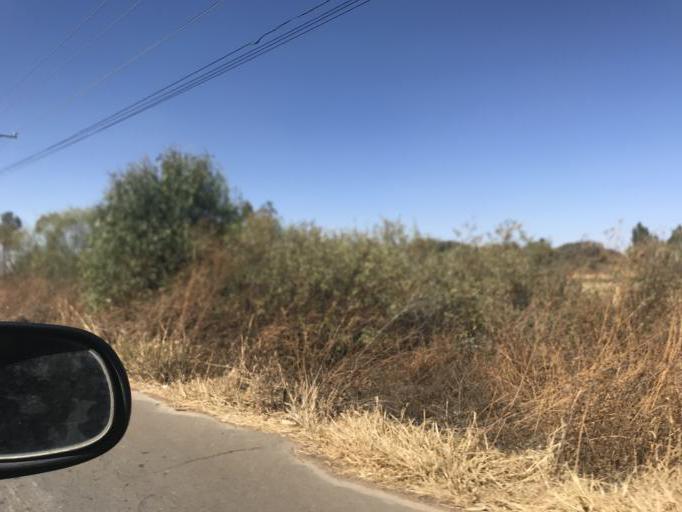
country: BO
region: Cochabamba
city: Tarata
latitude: -17.6047
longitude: -65.9921
